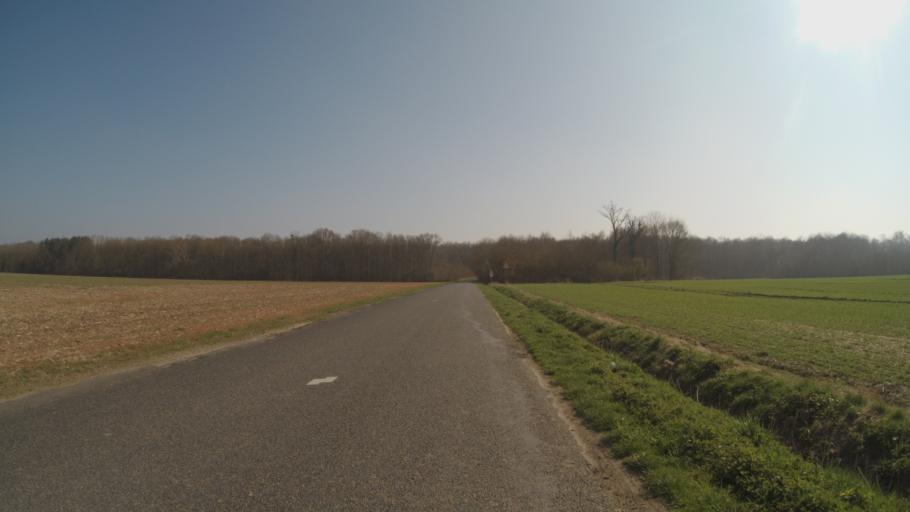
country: FR
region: Centre
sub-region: Departement du Loiret
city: Mardie
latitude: 47.9199
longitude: 2.0508
